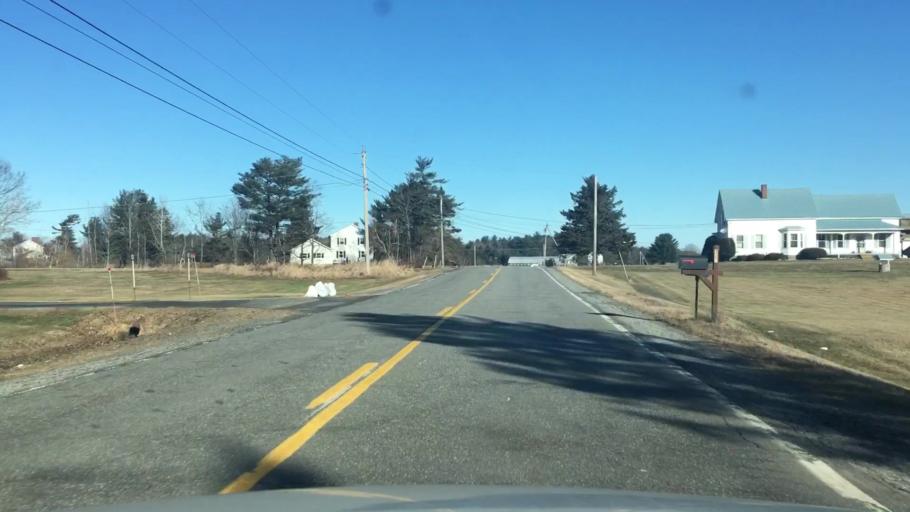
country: US
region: Maine
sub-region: Somerset County
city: Fairfield
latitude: 44.5634
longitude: -69.5778
